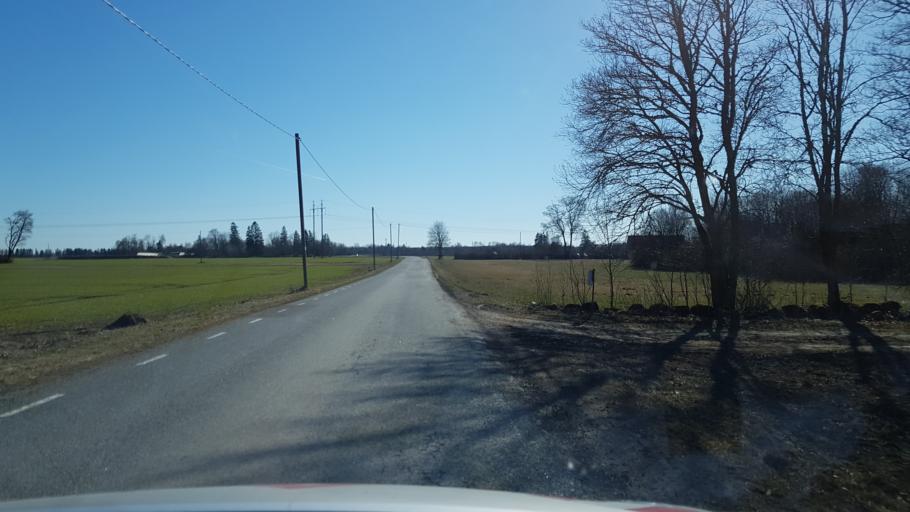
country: EE
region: Laeaene-Virumaa
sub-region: Someru vald
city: Someru
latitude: 59.3780
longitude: 26.4570
